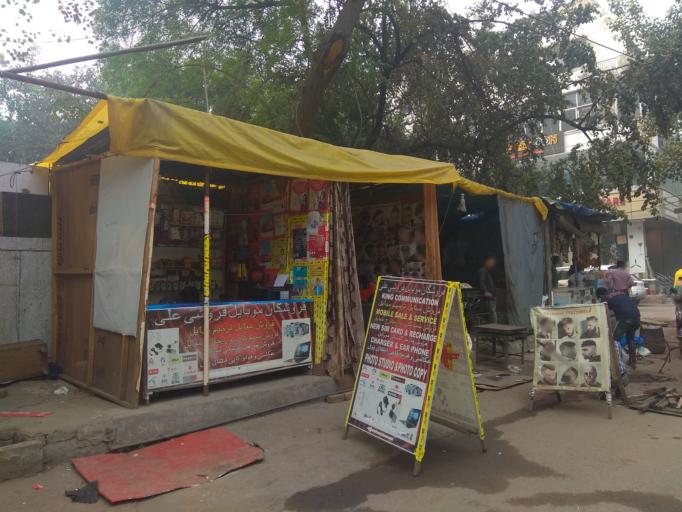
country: IN
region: NCT
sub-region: New Delhi
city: New Delhi
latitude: 28.5702
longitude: 77.2449
